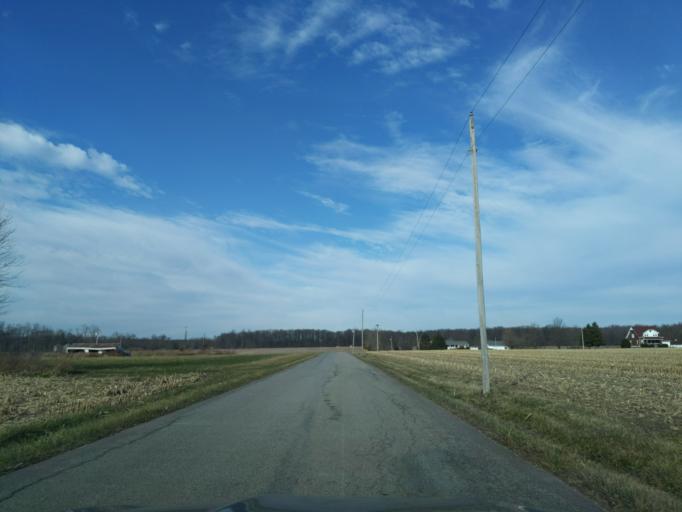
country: US
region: Indiana
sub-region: Decatur County
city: Greensburg
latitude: 39.2617
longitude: -85.4188
